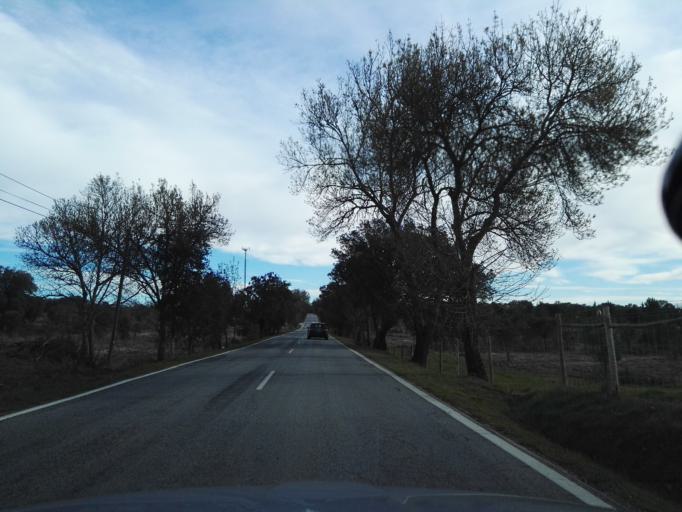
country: PT
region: Portalegre
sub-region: Nisa
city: Nisa
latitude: 39.4932
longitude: -7.7128
